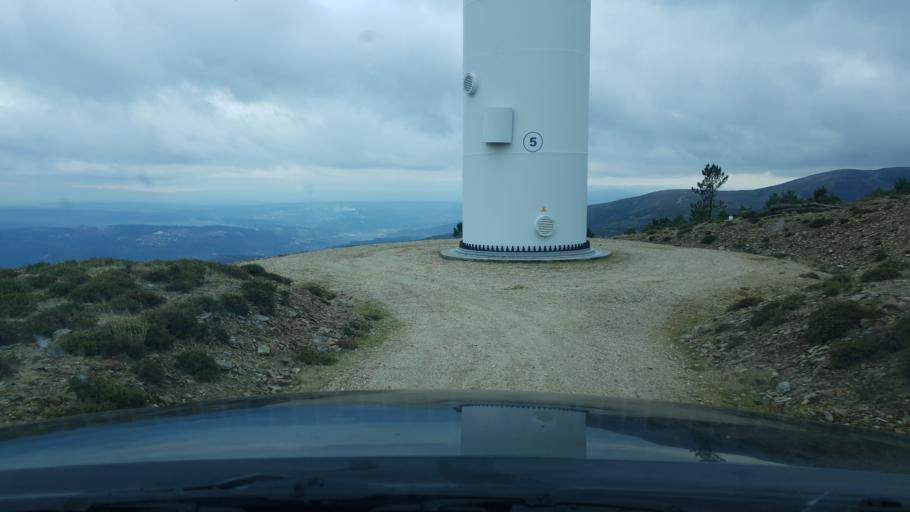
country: PT
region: Viseu
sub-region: Sao Pedro do Sul
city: Sao Pedro do Sul
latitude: 40.8648
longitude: -8.0820
